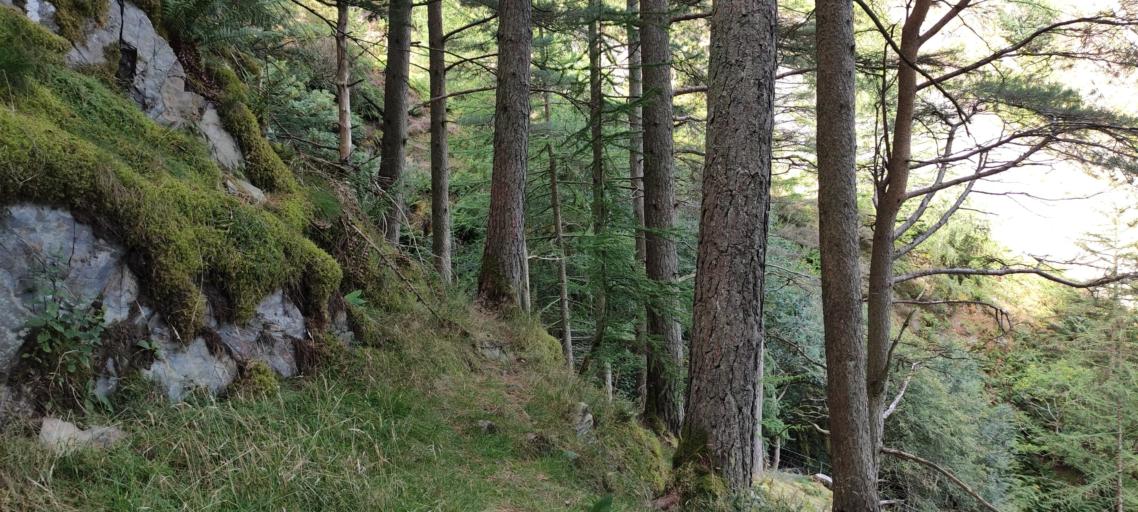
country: GB
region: England
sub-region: Cumbria
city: Keswick
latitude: 54.6267
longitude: -3.2181
